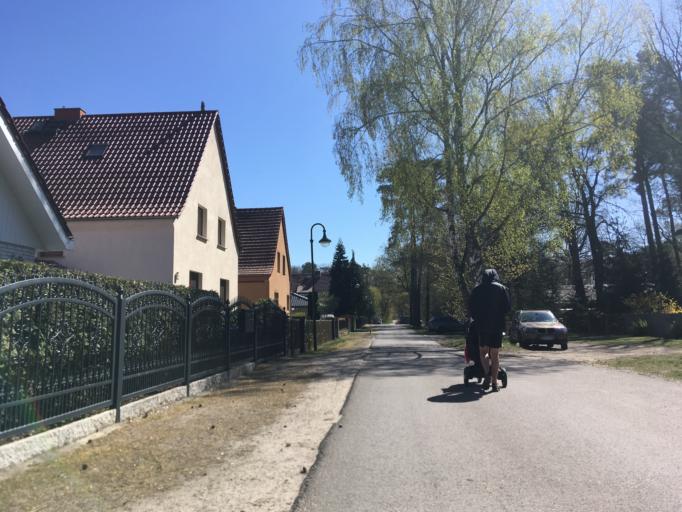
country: DE
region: Brandenburg
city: Bernau bei Berlin
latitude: 52.6967
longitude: 13.5455
